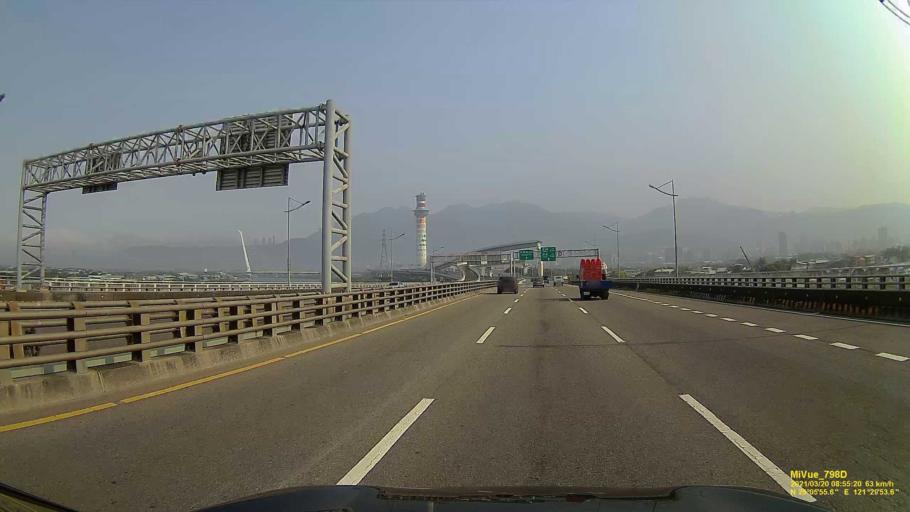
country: TW
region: Taipei
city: Taipei
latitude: 25.0978
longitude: 121.4994
